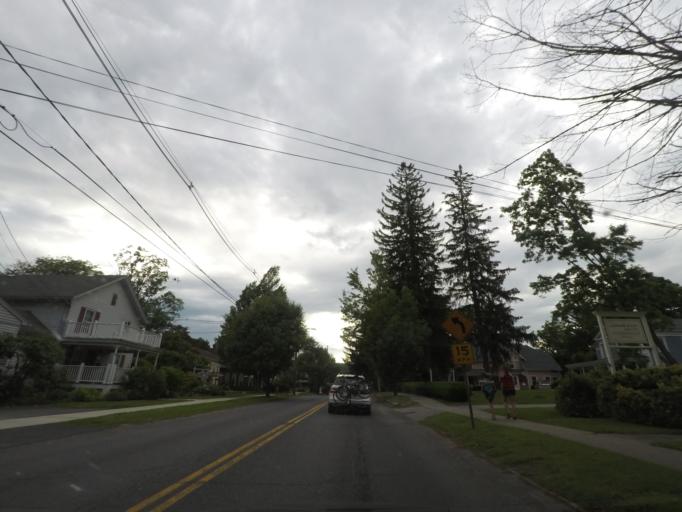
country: US
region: New York
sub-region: Dutchess County
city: Pine Plains
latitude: 41.9533
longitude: -73.5077
